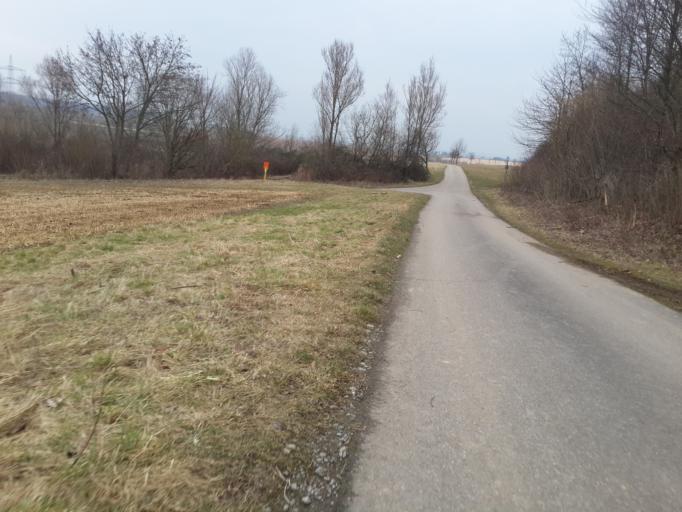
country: DE
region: Baden-Wuerttemberg
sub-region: Regierungsbezirk Stuttgart
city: Bad Wimpfen
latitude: 49.1852
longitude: 9.1585
